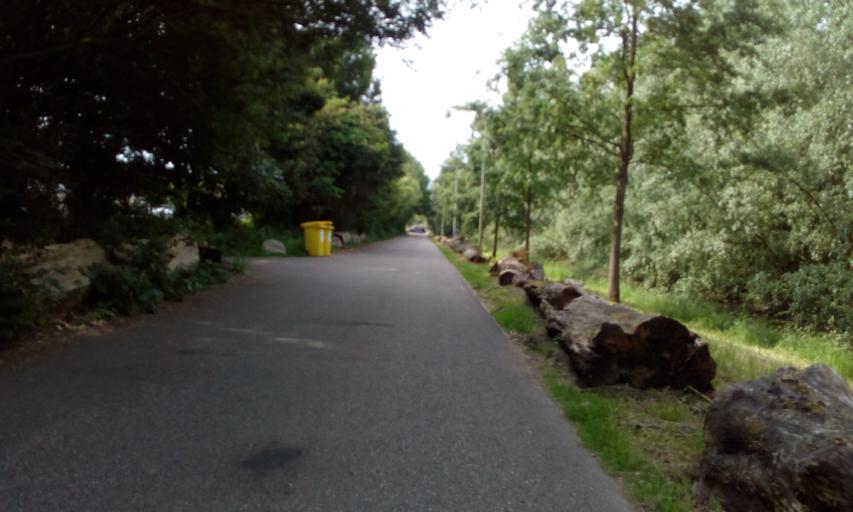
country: NL
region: South Holland
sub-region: Gemeente Rotterdam
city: Delfshaven
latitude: 51.9314
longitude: 4.4505
